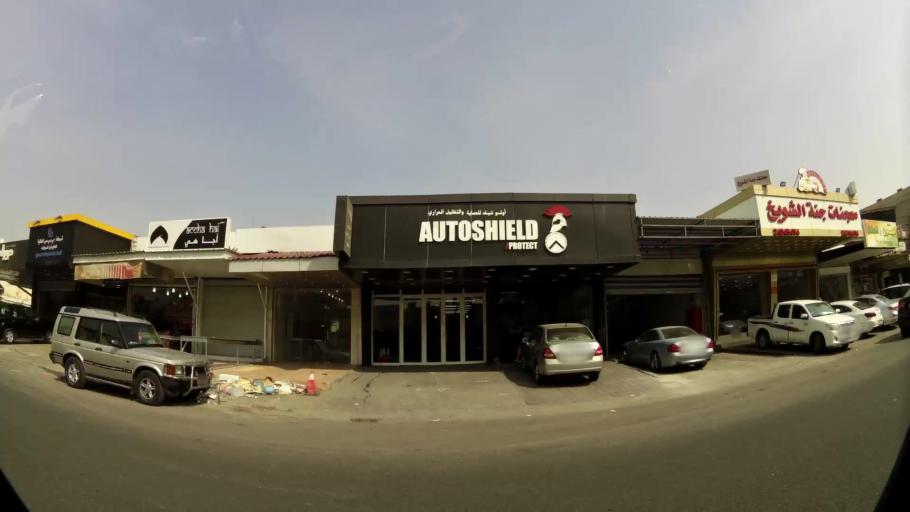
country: KW
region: Al Asimah
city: Ar Rabiyah
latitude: 29.3185
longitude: 47.9324
